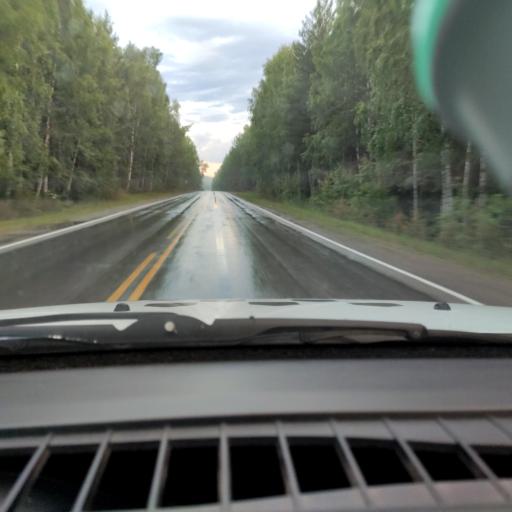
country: RU
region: Chelyabinsk
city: Kyshtym
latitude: 55.7487
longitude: 60.5504
